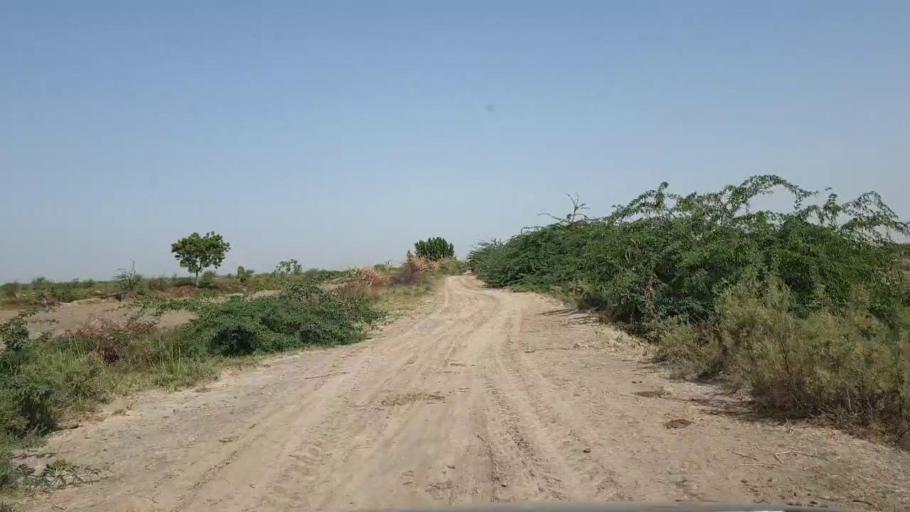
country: PK
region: Sindh
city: Tando Bago
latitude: 24.7023
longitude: 69.0708
